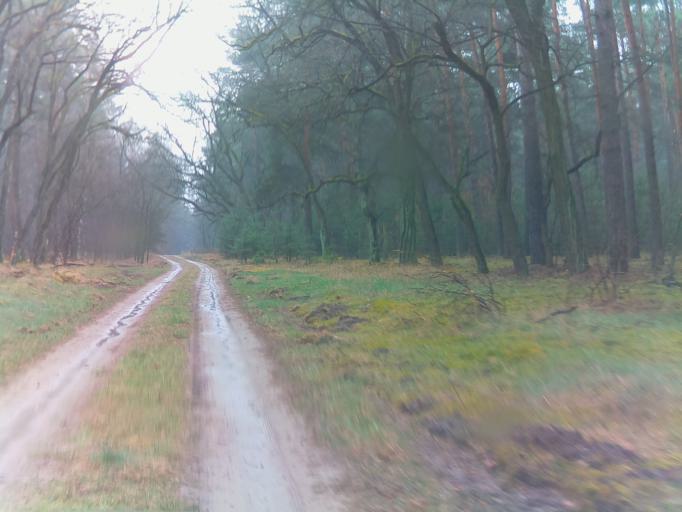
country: DE
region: Brandenburg
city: Jamlitz
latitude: 52.0459
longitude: 14.3631
